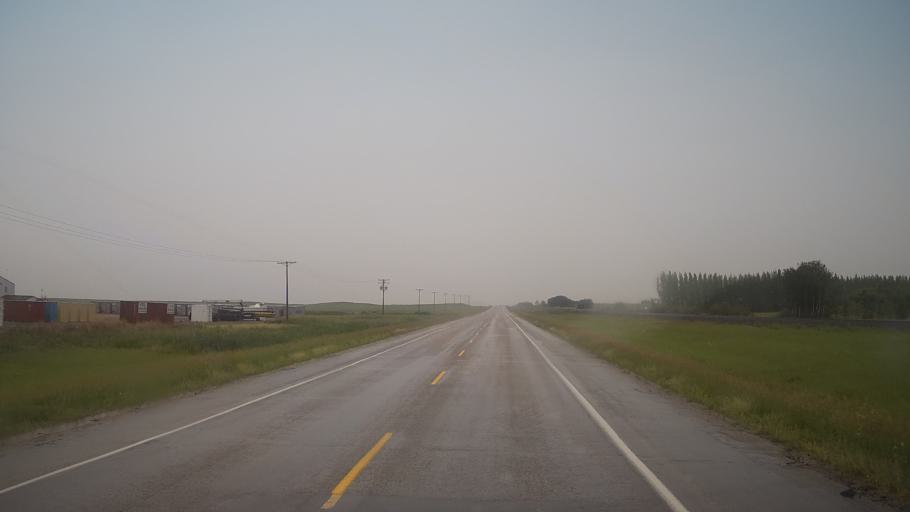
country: CA
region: Saskatchewan
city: Biggar
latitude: 52.0883
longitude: -108.0468
